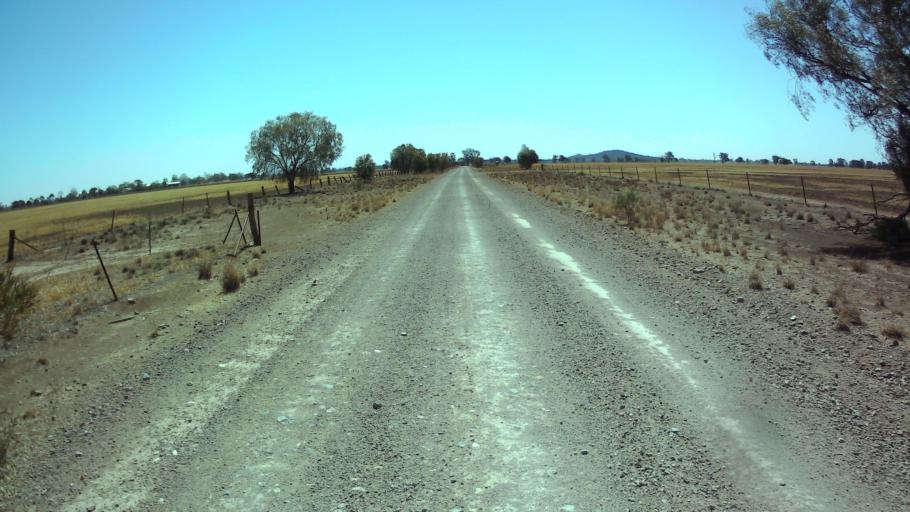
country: AU
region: New South Wales
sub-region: Forbes
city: Forbes
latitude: -33.7468
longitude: 147.7224
